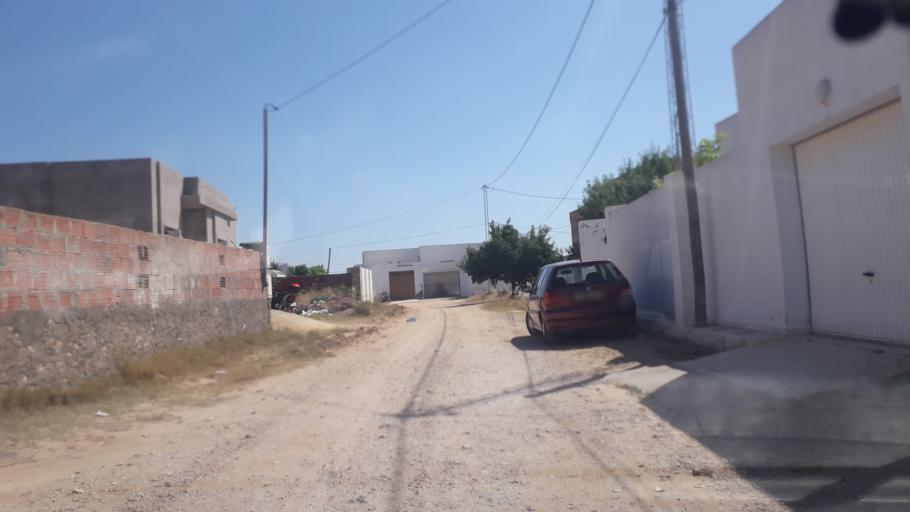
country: TN
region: Safaqis
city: Al Qarmadah
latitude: 34.8327
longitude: 10.7676
